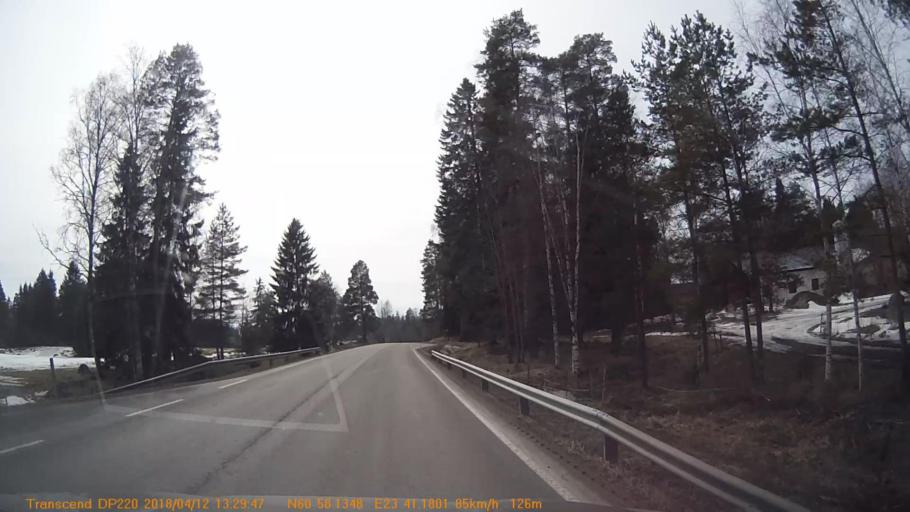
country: FI
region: Haeme
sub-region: Forssa
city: Forssa
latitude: 60.9688
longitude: 23.6861
